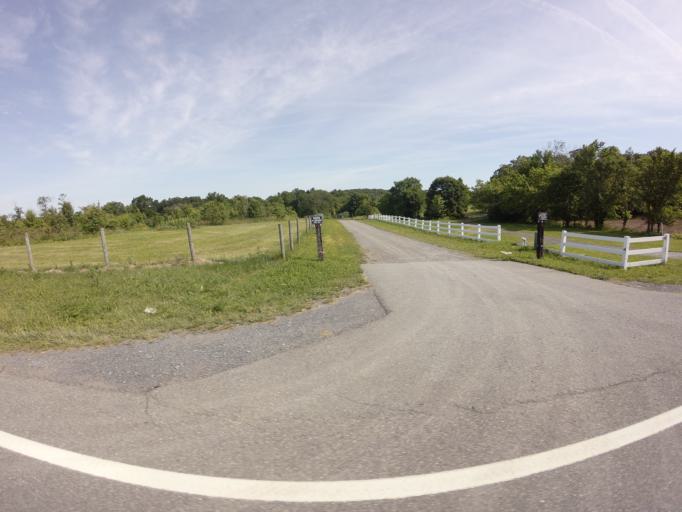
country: US
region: Maryland
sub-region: Frederick County
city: Green Valley
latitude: 39.3474
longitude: -77.2966
